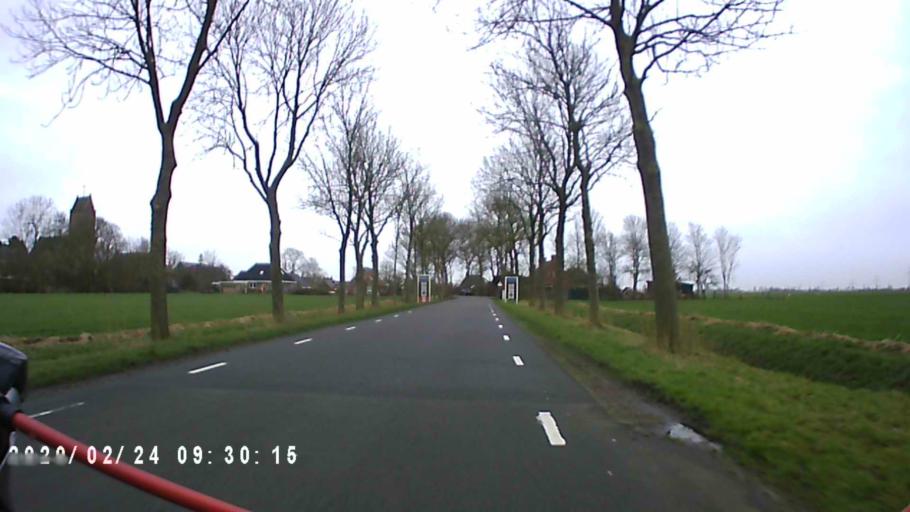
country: NL
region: Groningen
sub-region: Gemeente Winsum
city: Winsum
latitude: 53.3058
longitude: 6.4885
